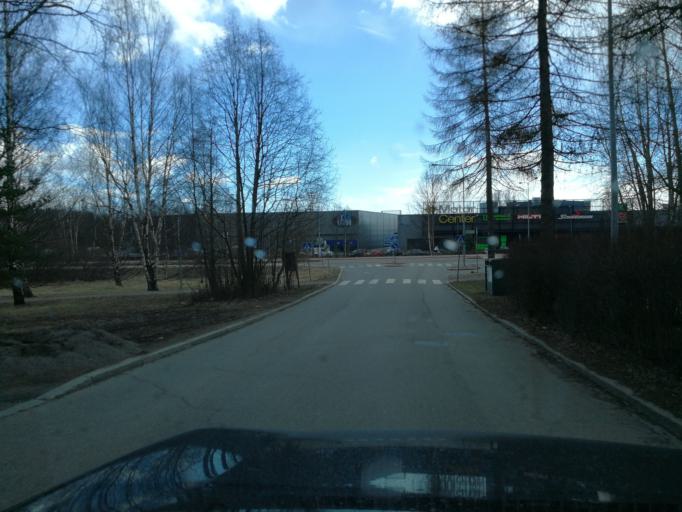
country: FI
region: Uusimaa
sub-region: Helsinki
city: Teekkarikylae
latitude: 60.2432
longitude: 24.8427
